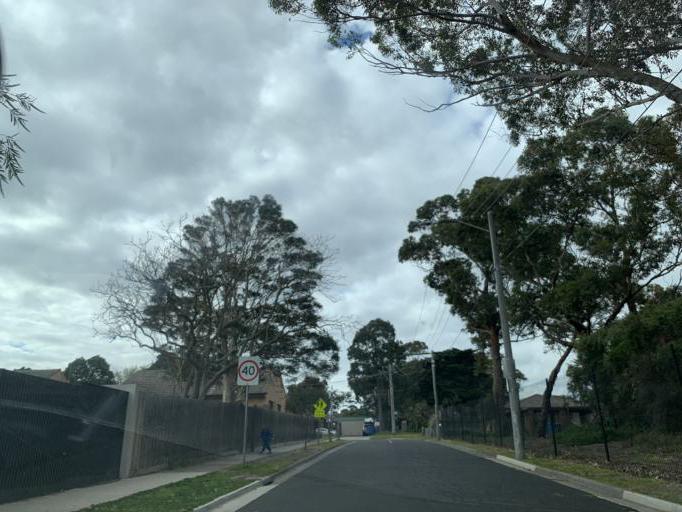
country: AU
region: Victoria
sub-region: Bayside
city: Black Rock
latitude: -37.9707
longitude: 145.0220
